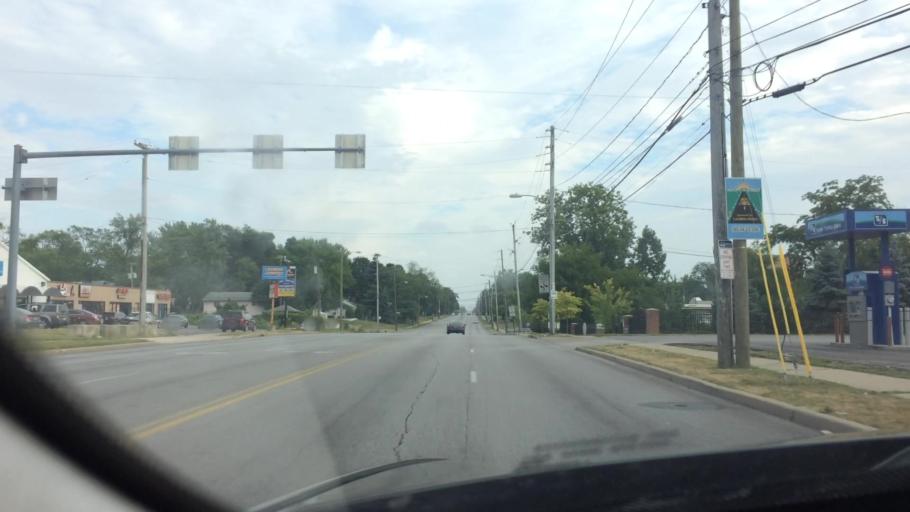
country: US
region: Ohio
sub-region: Lucas County
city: Ottawa Hills
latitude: 41.6525
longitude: -83.6260
